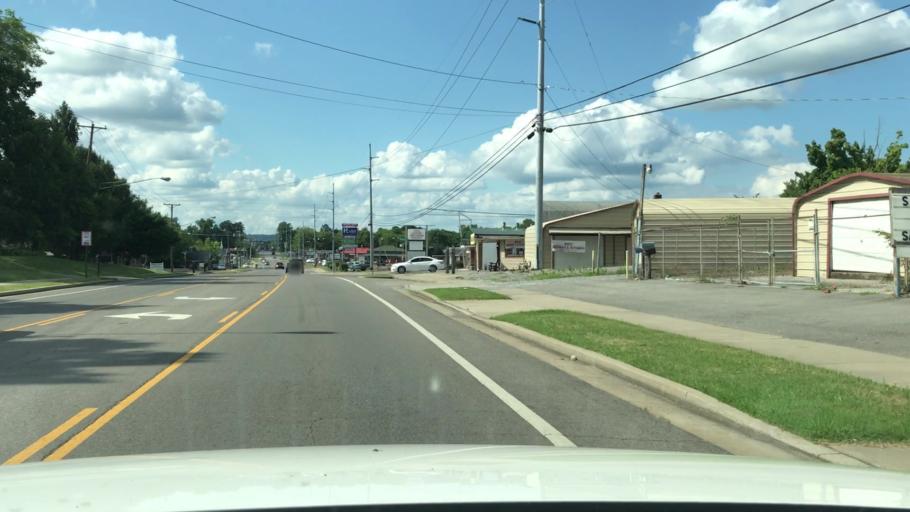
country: US
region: Tennessee
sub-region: Sumner County
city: Gallatin
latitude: 36.3764
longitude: -86.4418
